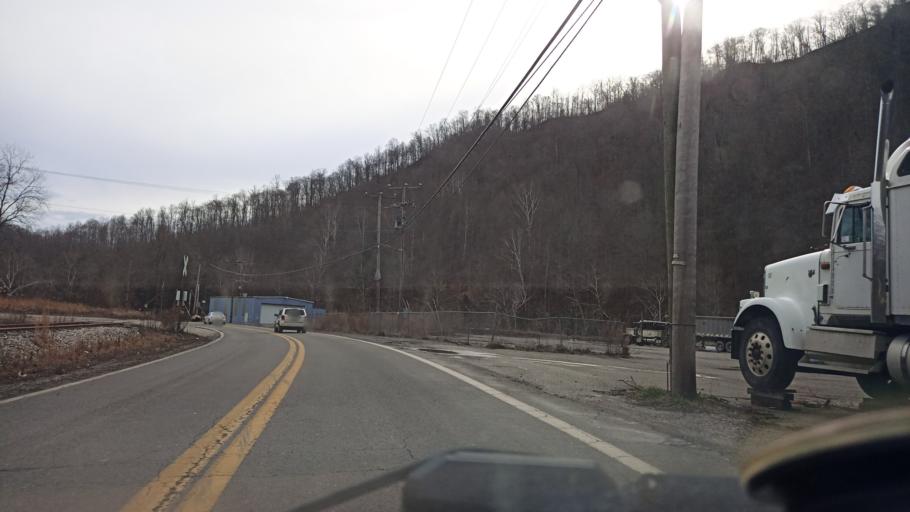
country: US
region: West Virginia
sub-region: Mingo County
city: Gilbert Creek
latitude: 37.6231
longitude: -81.8690
